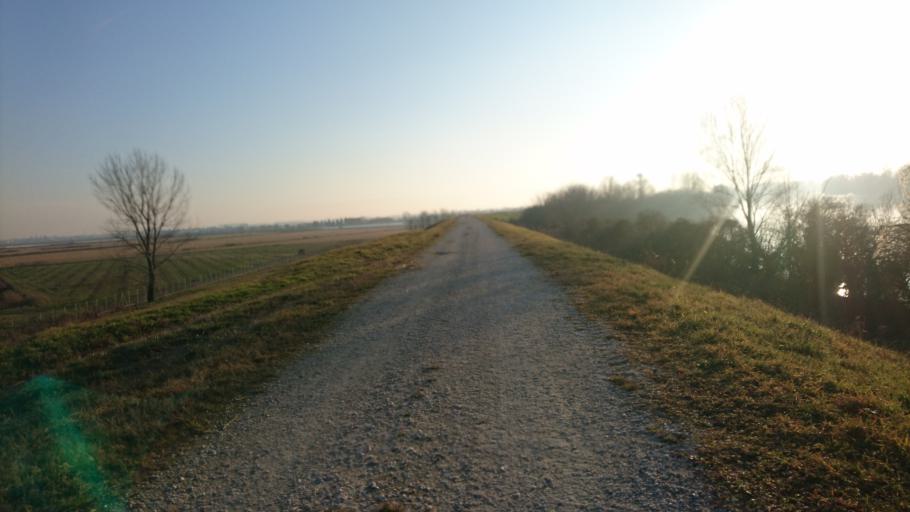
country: IT
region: Veneto
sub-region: Provincia di Padova
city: Boara Pisani
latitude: 45.1189
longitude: 11.8062
